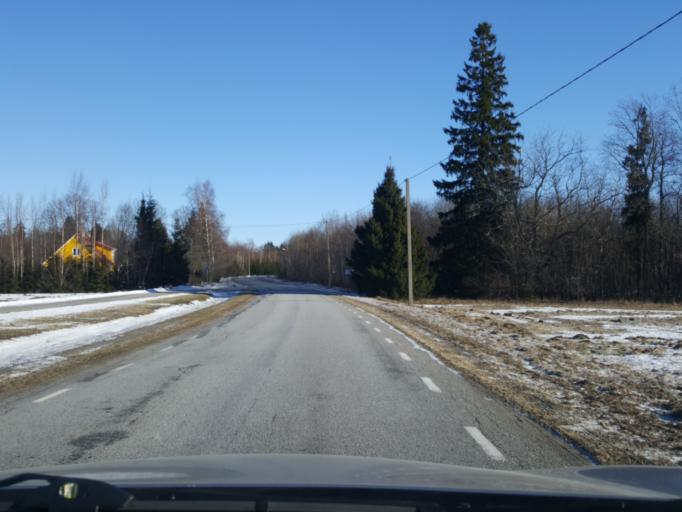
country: EE
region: Viljandimaa
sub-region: Suure-Jaani vald
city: Suure-Jaani
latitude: 58.5441
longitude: 25.5365
